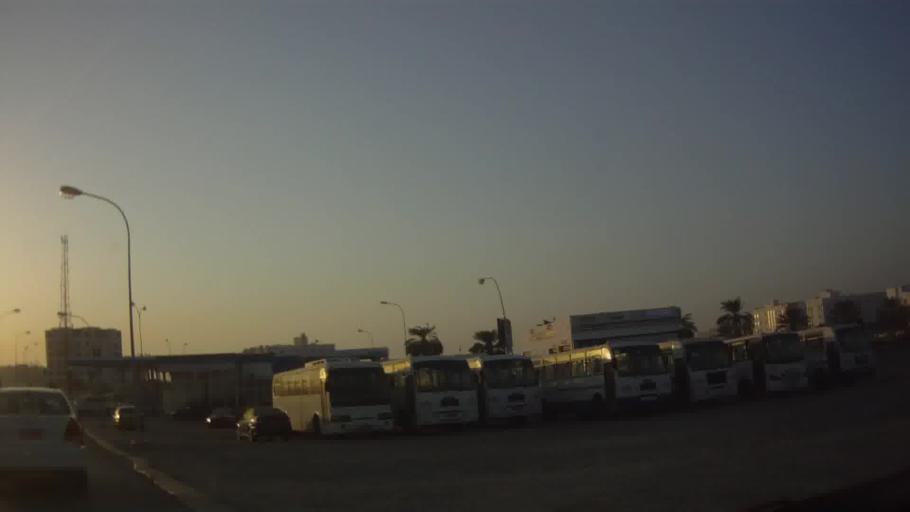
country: OM
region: Muhafazat Masqat
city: Bawshar
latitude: 23.5927
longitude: 58.4118
